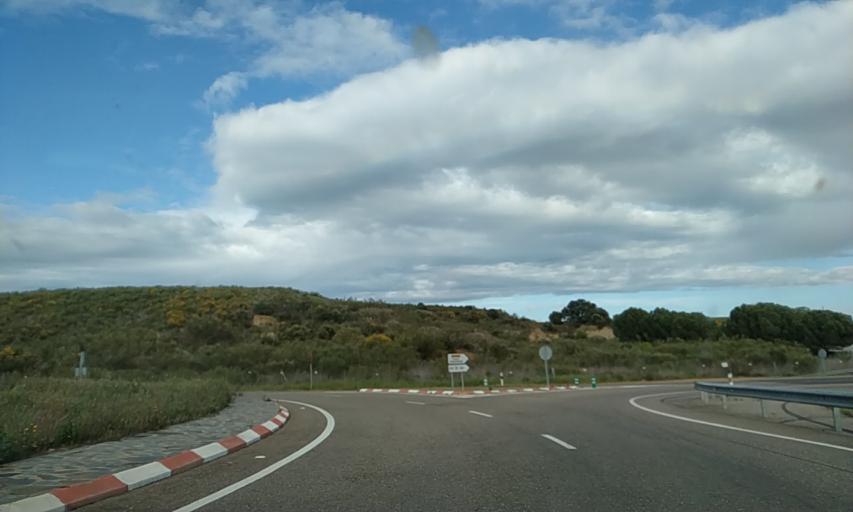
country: ES
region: Extremadura
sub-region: Provincia de Caceres
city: Coria
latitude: 40.0086
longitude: -6.5607
